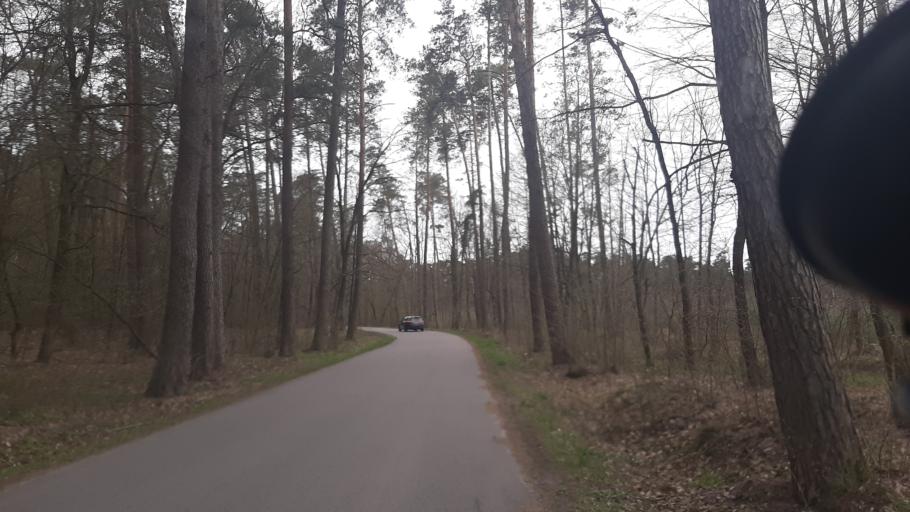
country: PL
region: Lublin Voivodeship
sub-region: Powiat lubelski
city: Niemce
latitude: 51.3768
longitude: 22.5532
